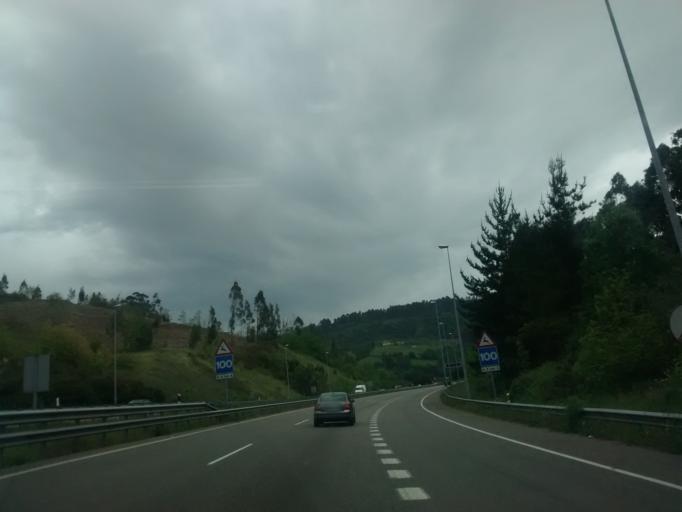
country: ES
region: Asturias
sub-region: Province of Asturias
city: Arriba
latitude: 43.5095
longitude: -5.5967
